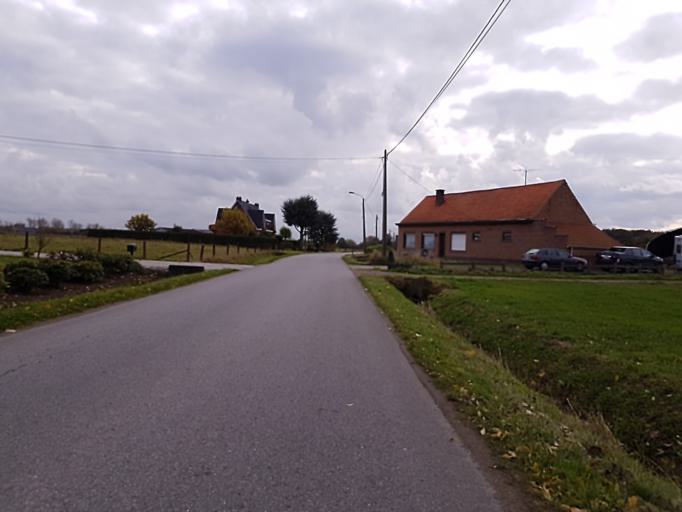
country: BE
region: Flanders
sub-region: Provincie Antwerpen
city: Lint
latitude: 51.1285
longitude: 4.5322
